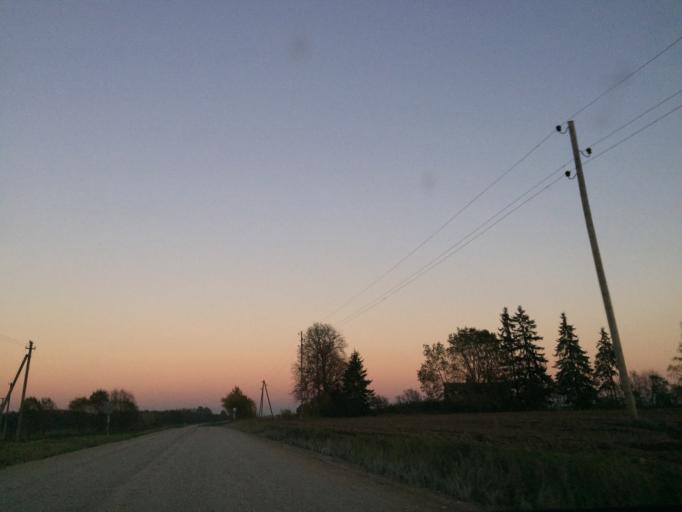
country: LT
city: Akmene
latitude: 56.3774
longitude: 22.6710
